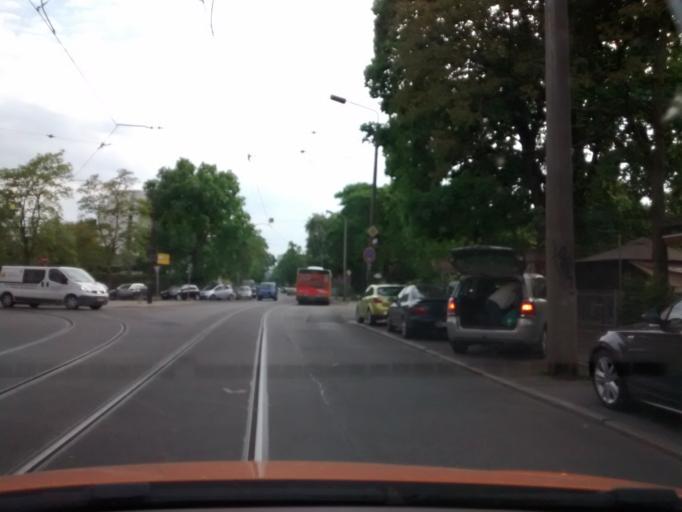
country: DE
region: Berlin
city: Johannisthal
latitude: 52.4455
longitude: 13.5053
